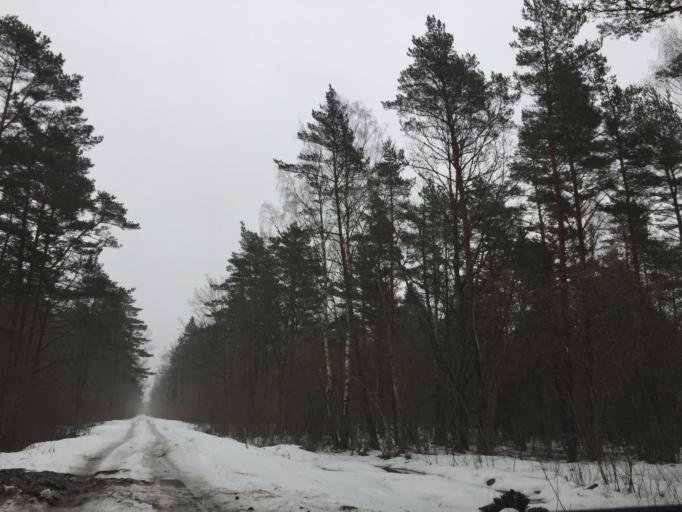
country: EE
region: Saare
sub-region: Kuressaare linn
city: Kuressaare
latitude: 58.2706
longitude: 22.5533
